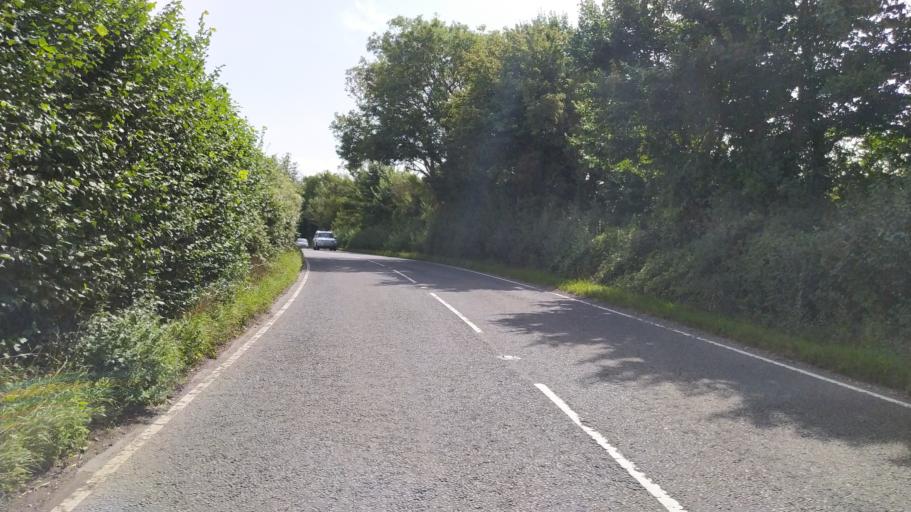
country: GB
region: England
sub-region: Dorset
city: Blandford Forum
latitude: 50.8954
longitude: -2.1935
